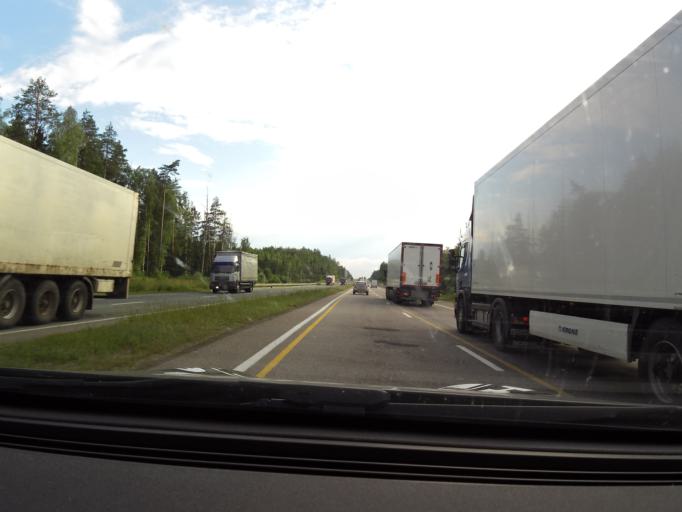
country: RU
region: Vladimir
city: Sudogda
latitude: 56.1461
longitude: 40.9102
